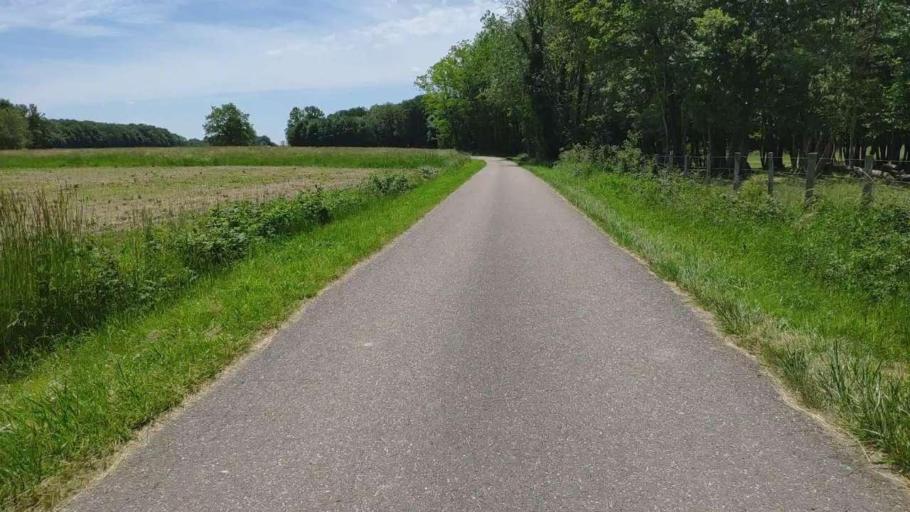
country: FR
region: Franche-Comte
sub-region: Departement du Jura
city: Bletterans
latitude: 46.7782
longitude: 5.3761
